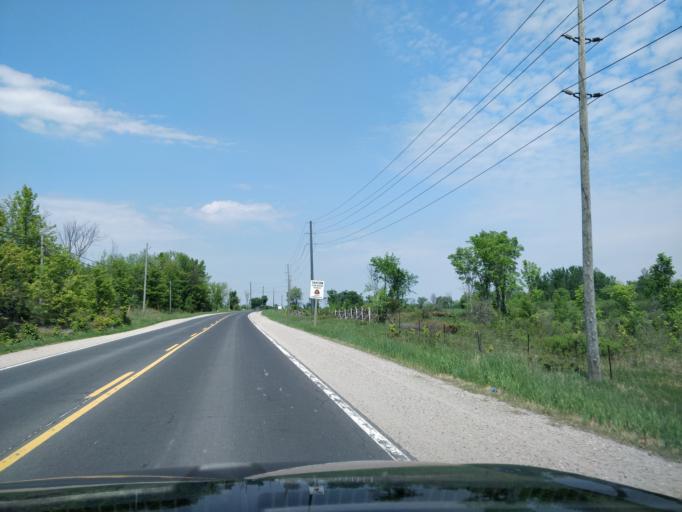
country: CA
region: Ontario
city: Perth
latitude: 44.8302
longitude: -76.3133
